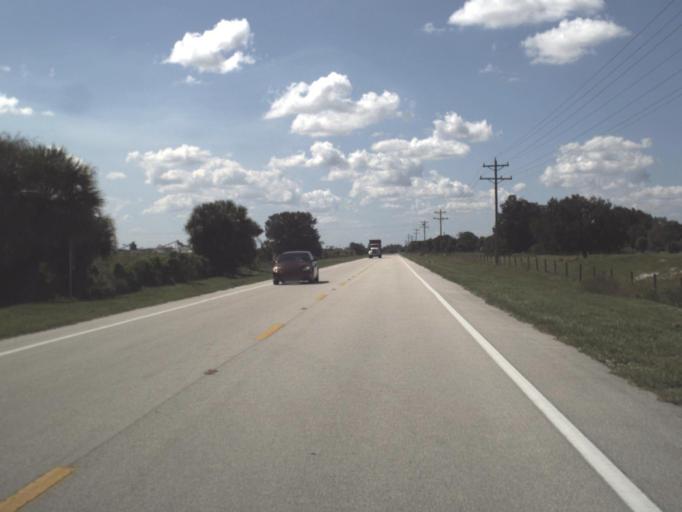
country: US
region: Florida
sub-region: Hendry County
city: Port LaBelle
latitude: 26.8124
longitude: -81.2640
